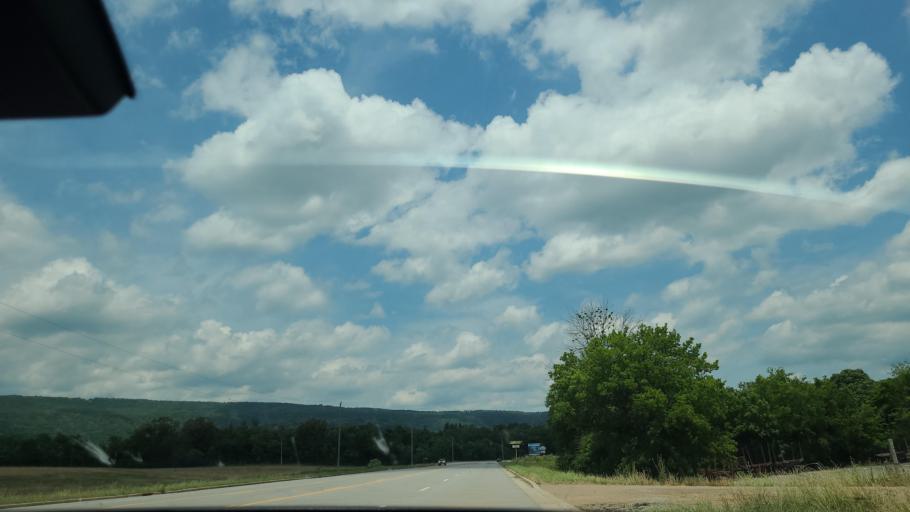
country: US
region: Tennessee
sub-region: Bledsoe County
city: Pikeville
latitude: 35.6026
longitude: -85.1966
